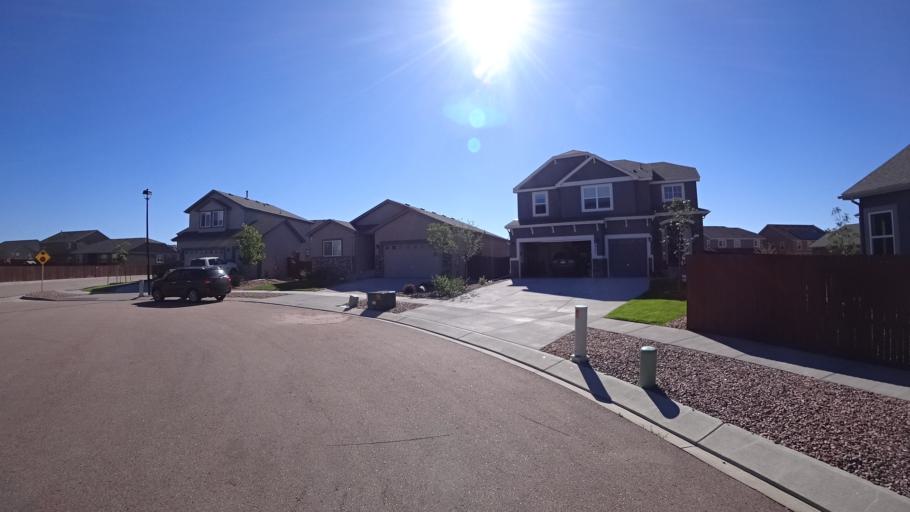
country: US
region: Colorado
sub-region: El Paso County
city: Black Forest
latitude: 38.9479
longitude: -104.6758
